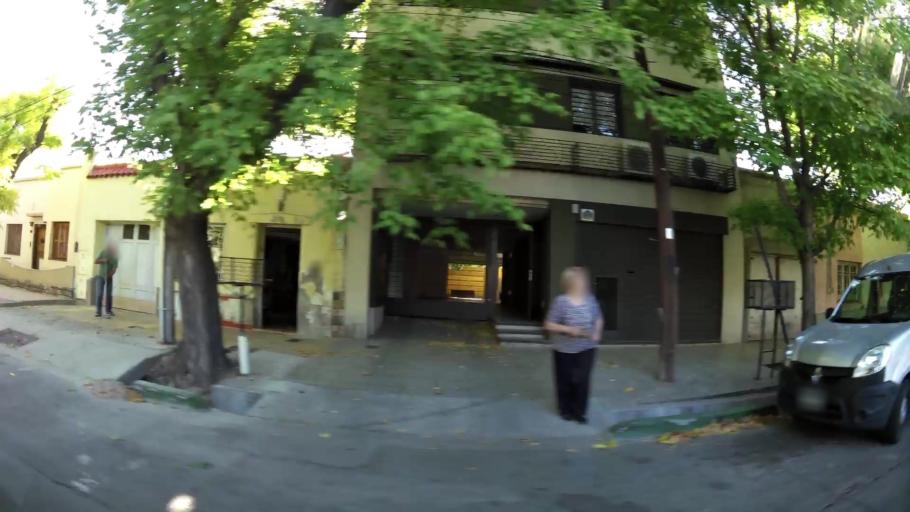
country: AR
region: Mendoza
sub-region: Departamento de Godoy Cruz
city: Godoy Cruz
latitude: -32.9245
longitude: -68.8497
